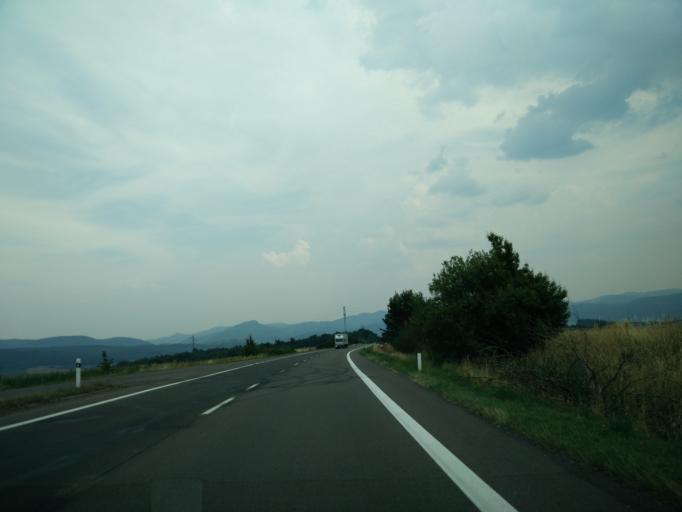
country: SK
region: Banskobystricky
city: Ziar nad Hronom
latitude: 48.6176
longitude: 18.8123
